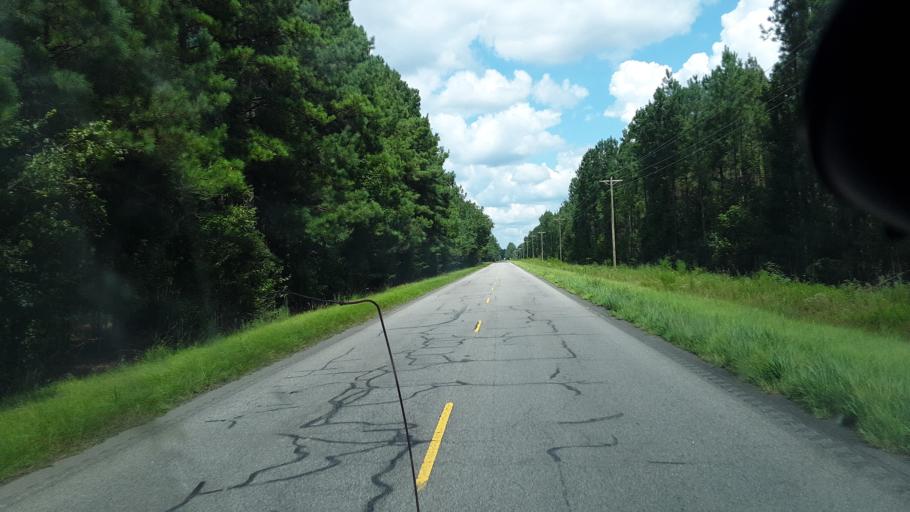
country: US
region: South Carolina
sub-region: Williamsburg County
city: Andrews
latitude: 33.5482
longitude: -79.4694
